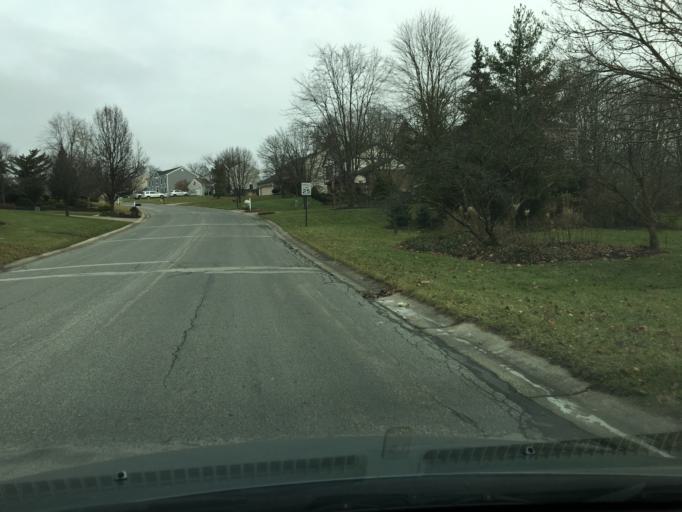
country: US
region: Ohio
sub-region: Hamilton County
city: Sharonville
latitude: 39.3076
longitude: -84.4012
